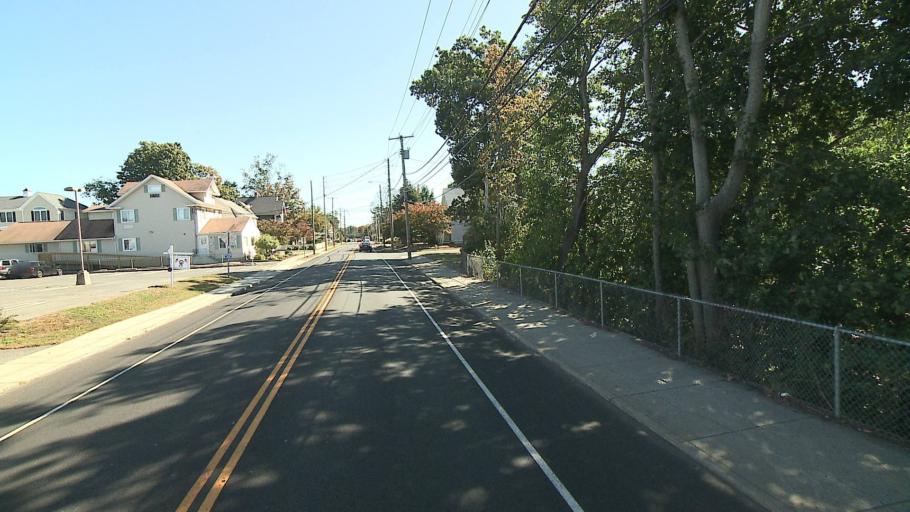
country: US
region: Connecticut
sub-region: New Haven County
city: Milford
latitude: 41.2230
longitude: -73.0524
